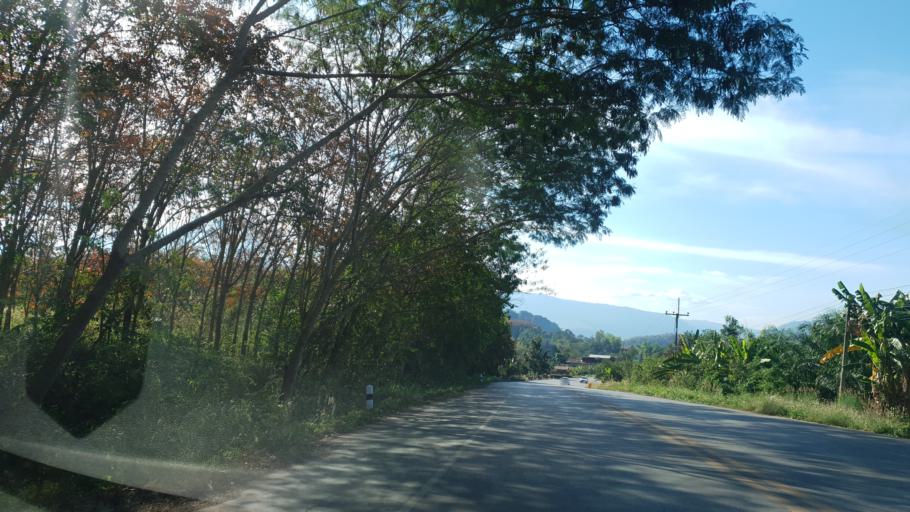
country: TH
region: Loei
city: Wang Saphung
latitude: 17.3331
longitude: 101.6702
